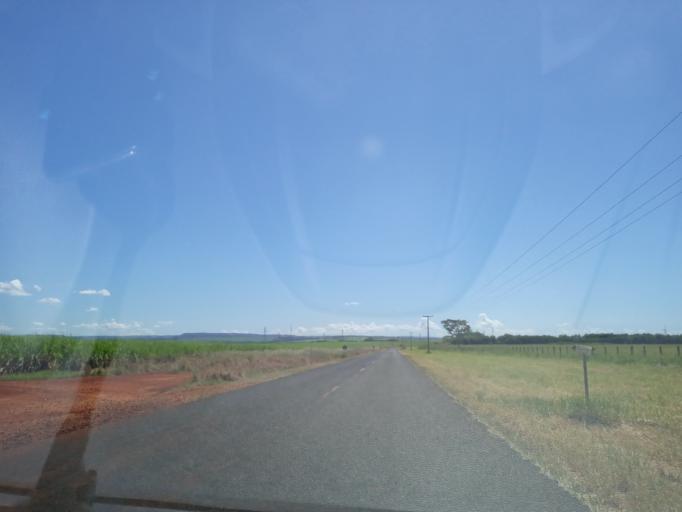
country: BR
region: Goias
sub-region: Itumbiara
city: Itumbiara
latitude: -18.4094
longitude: -49.1268
